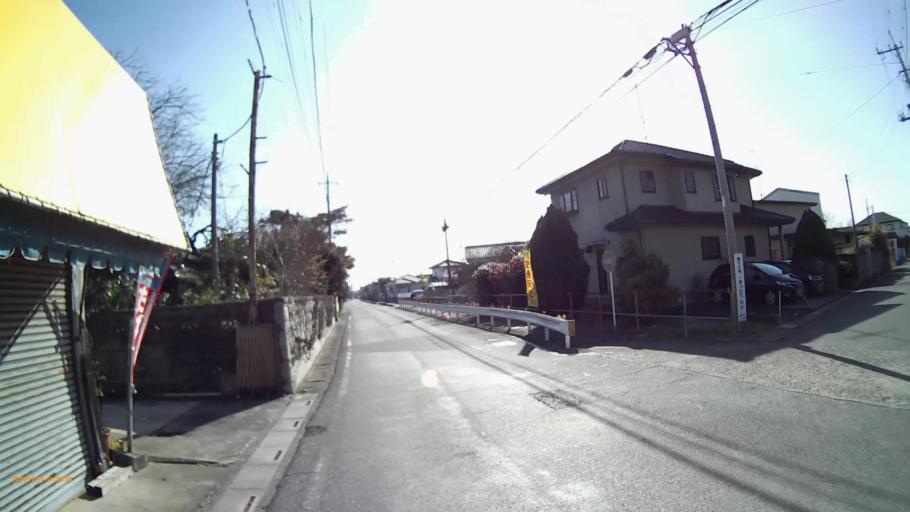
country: JP
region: Saitama
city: Kumagaya
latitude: 36.1292
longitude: 139.4010
